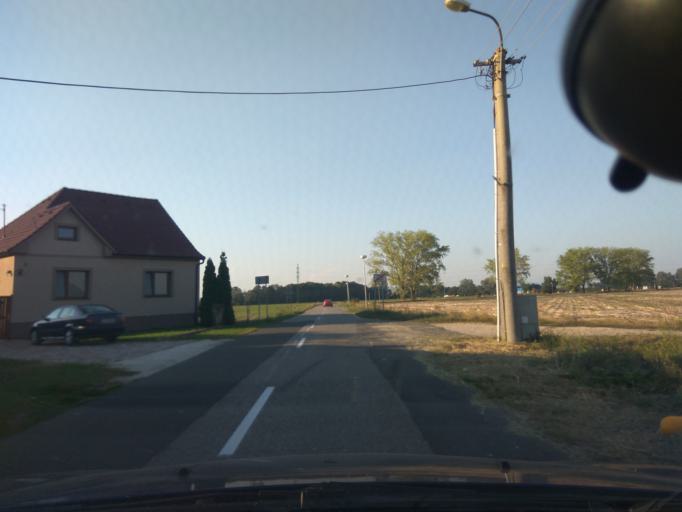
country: SK
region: Trnavsky
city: Vrbove
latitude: 48.5845
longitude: 17.7649
